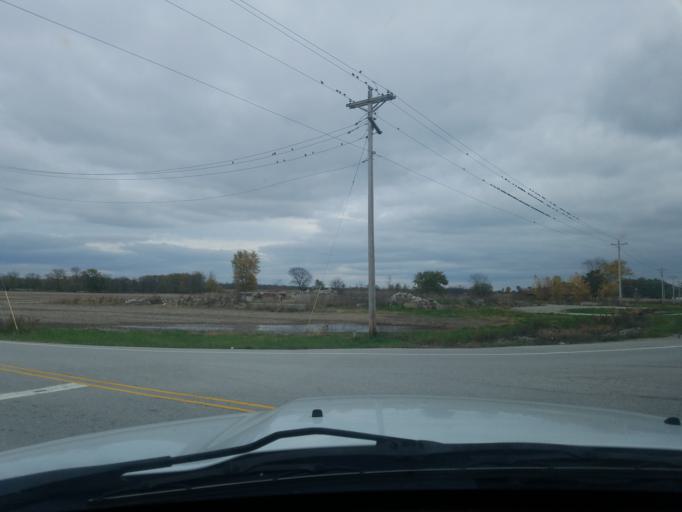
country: US
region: Indiana
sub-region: Shelby County
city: Shelbyville
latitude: 39.4959
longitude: -85.8946
